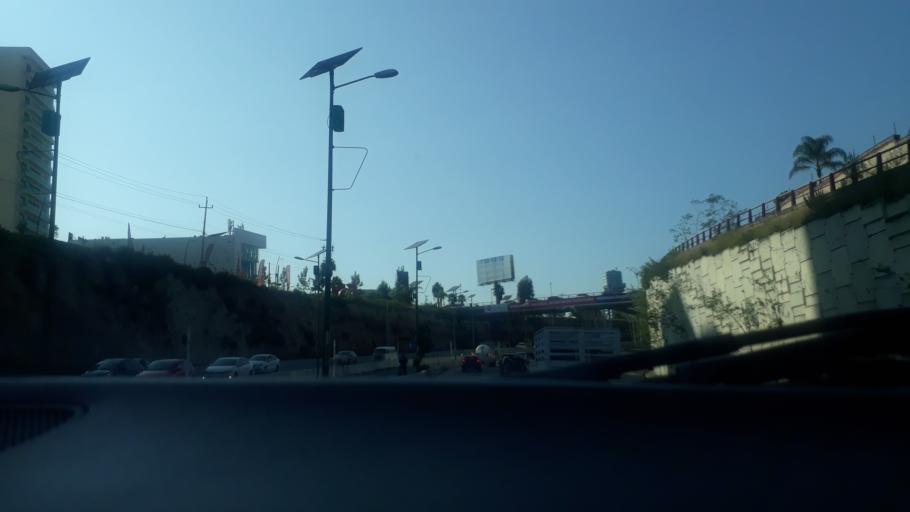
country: MX
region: Puebla
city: Tlazcalancingo
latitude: 18.9991
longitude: -98.2593
